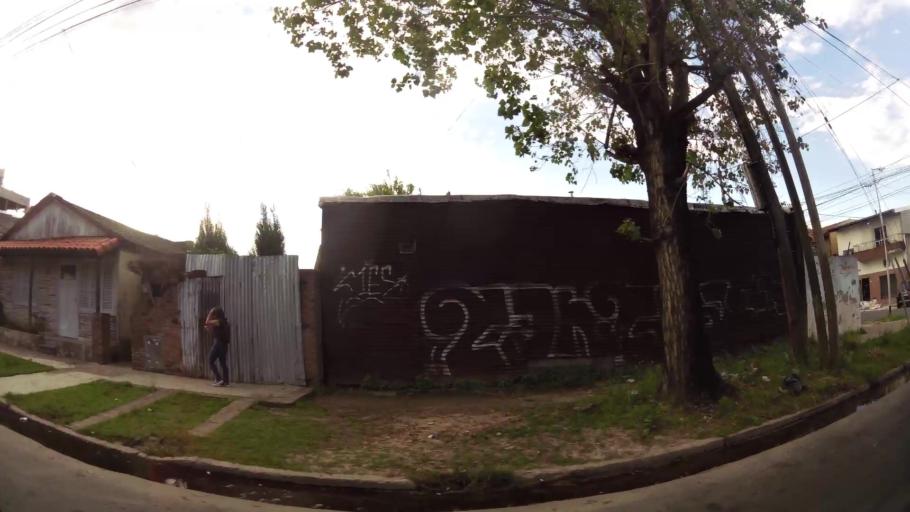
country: AR
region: Buenos Aires
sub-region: Partido de Avellaneda
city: Avellaneda
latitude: -34.6824
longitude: -58.3532
